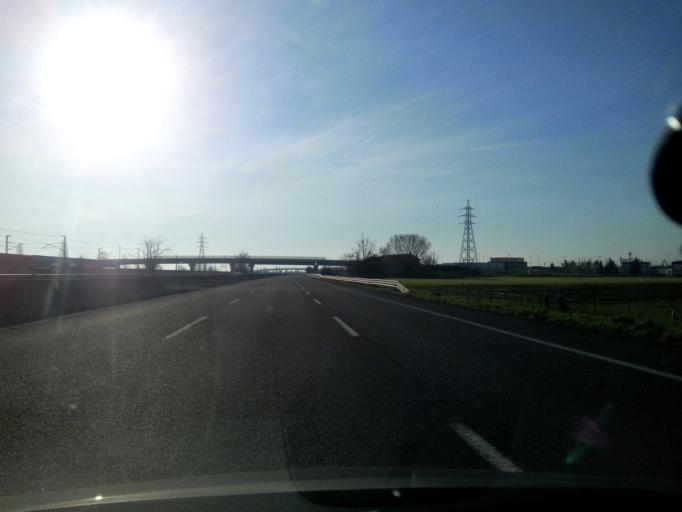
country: IT
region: Emilia-Romagna
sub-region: Provincia di Reggio Emilia
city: Praticello
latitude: 44.7980
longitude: 10.4558
